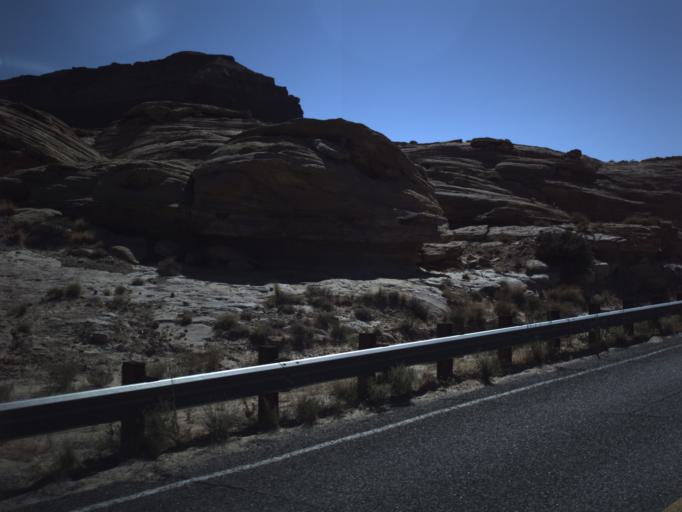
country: US
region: Utah
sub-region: San Juan County
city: Blanding
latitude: 37.9147
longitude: -110.3881
